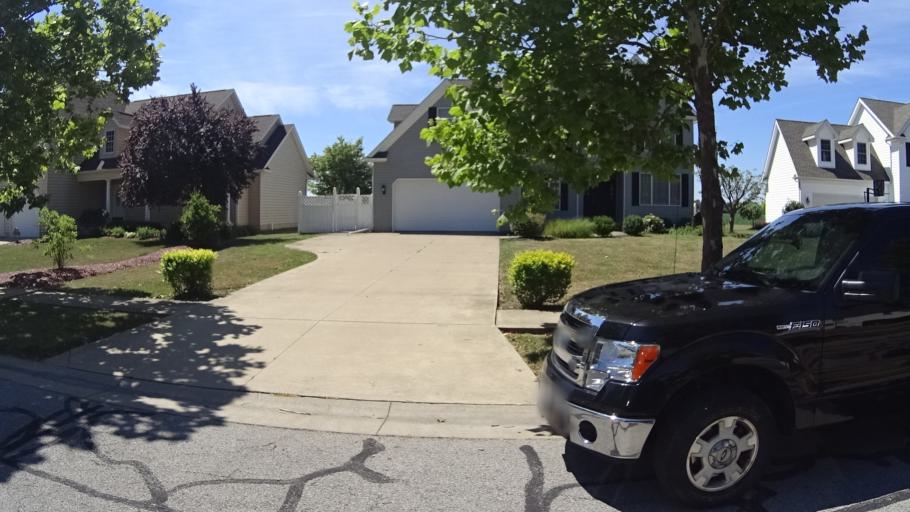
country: US
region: Ohio
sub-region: Erie County
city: Sandusky
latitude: 41.4047
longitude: -82.6994
